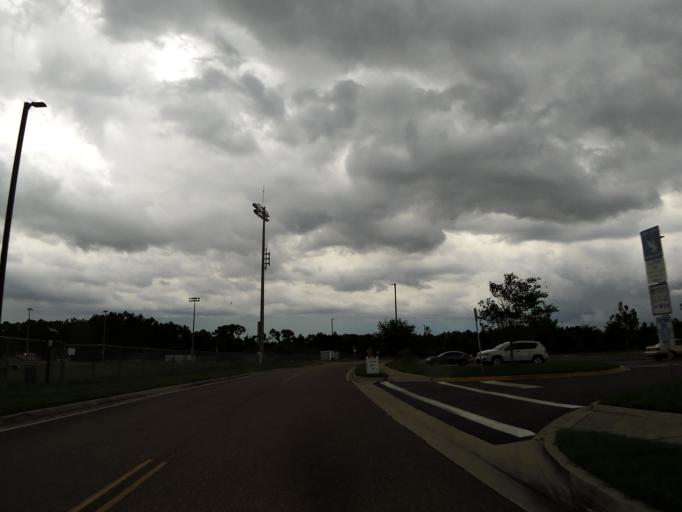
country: US
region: Florida
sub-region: Duval County
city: Jacksonville Beach
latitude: 30.2774
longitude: -81.5124
